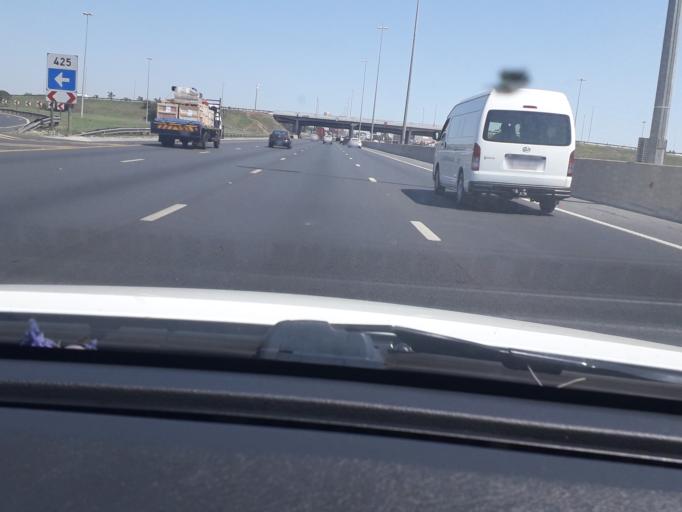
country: ZA
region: Gauteng
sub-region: Ekurhuleni Metropolitan Municipality
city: Germiston
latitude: -26.1772
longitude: 28.2006
